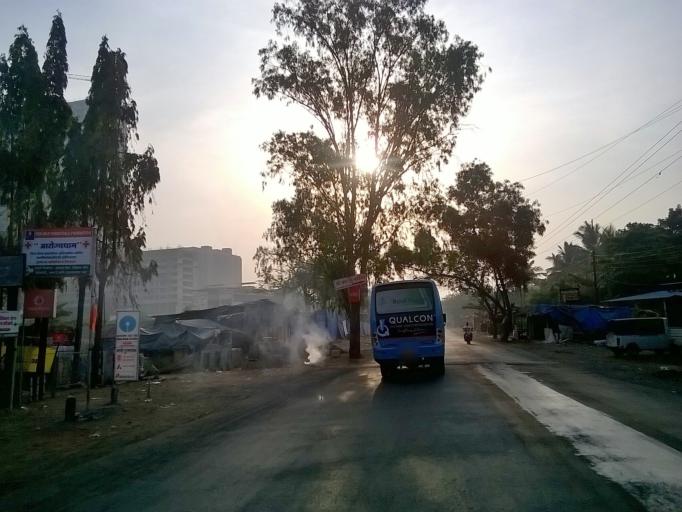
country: IN
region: Maharashtra
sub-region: Raigarh
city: Kalundri
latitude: 19.0004
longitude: 73.1318
